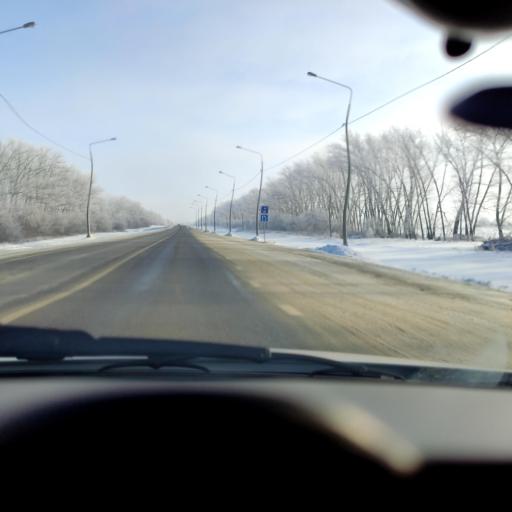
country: RU
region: Belgorod
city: Troitskiy
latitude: 51.6184
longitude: 37.5382
